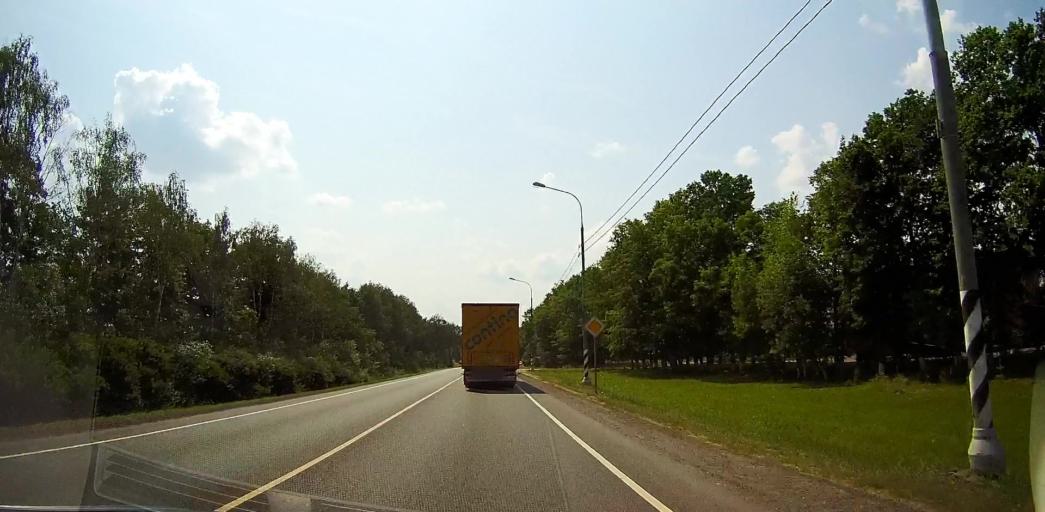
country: RU
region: Moskovskaya
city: Meshcherino
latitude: 55.1958
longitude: 38.3676
